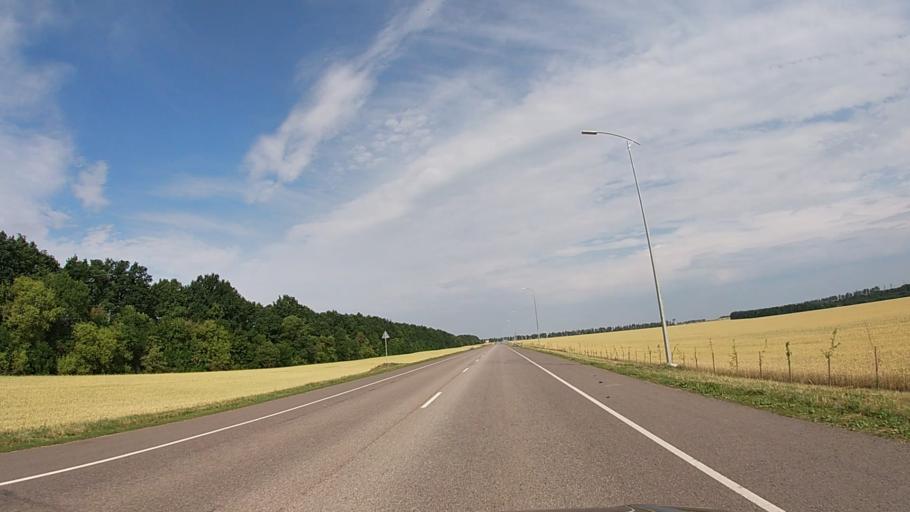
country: RU
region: Belgorod
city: Proletarskiy
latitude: 50.8258
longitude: 35.7795
